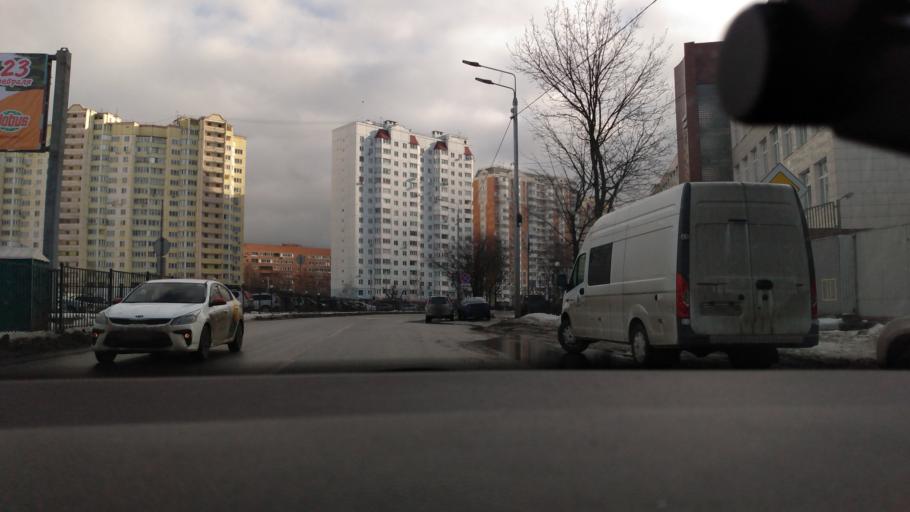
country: RU
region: Moskovskaya
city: Balashikha
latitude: 55.8296
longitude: 37.9530
